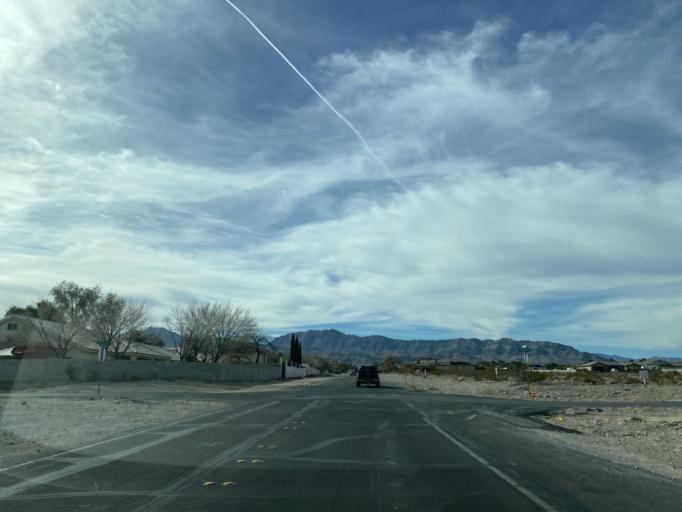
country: US
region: Nevada
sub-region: Clark County
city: Summerlin South
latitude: 36.2701
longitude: -115.2924
